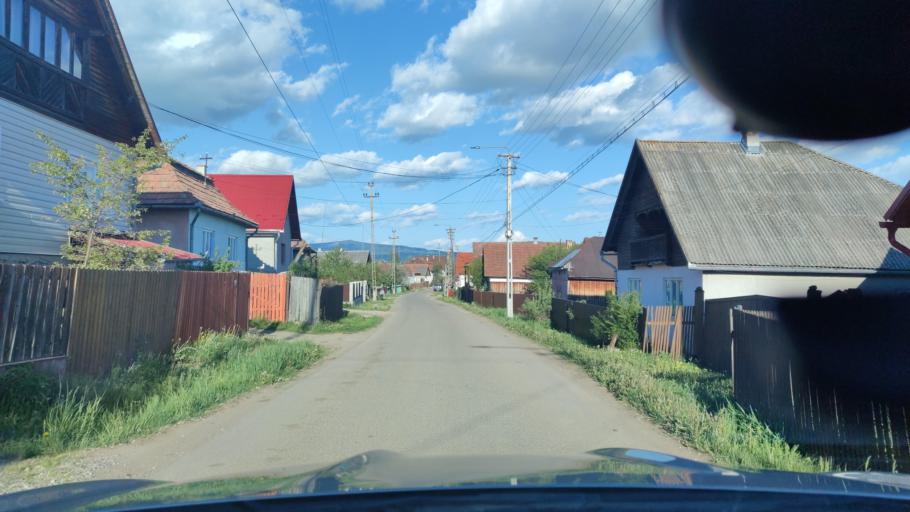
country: RO
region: Harghita
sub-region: Comuna Remetea
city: Remetea
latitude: 46.7996
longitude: 25.4274
